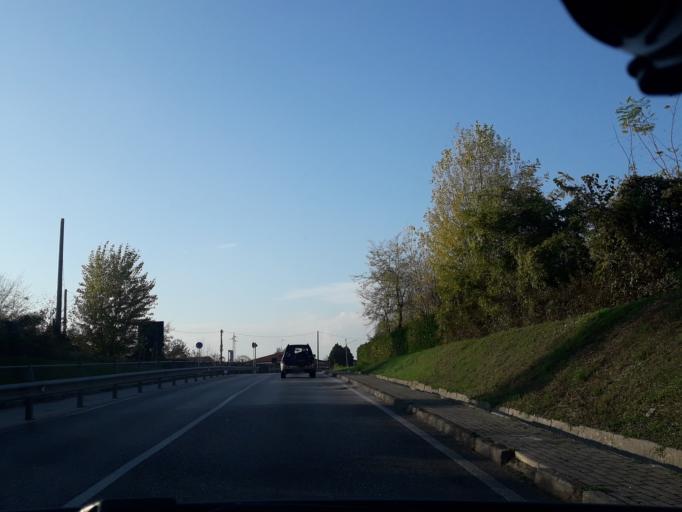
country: IT
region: Friuli Venezia Giulia
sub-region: Provincia di Udine
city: Udine
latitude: 46.0483
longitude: 13.2704
